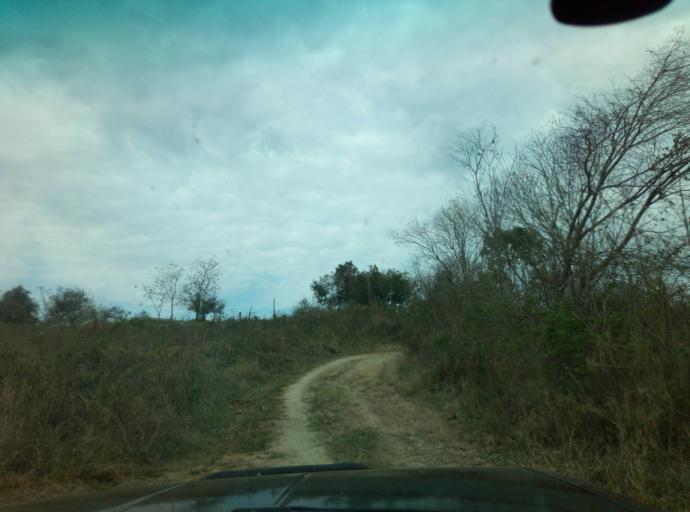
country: PY
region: Caaguazu
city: Doctor Cecilio Baez
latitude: -25.1993
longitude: -56.1268
